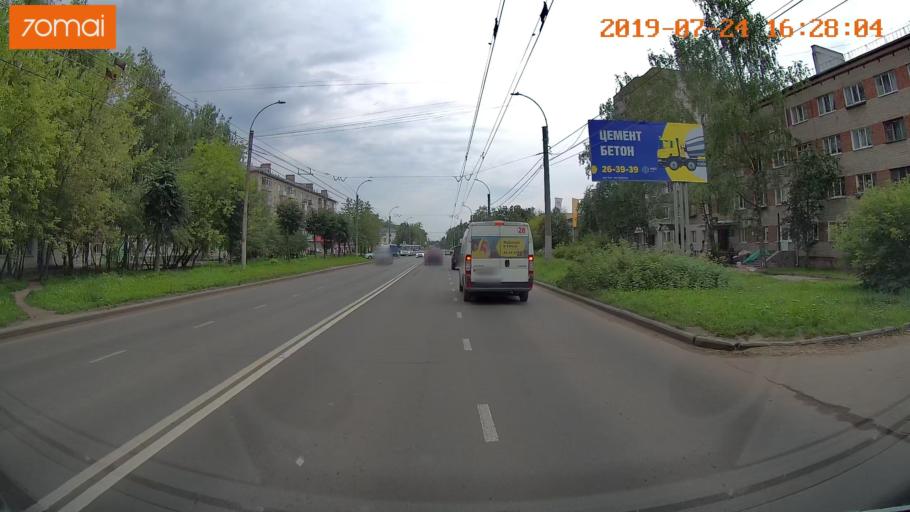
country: RU
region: Ivanovo
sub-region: Gorod Ivanovo
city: Ivanovo
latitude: 56.9744
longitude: 40.9650
